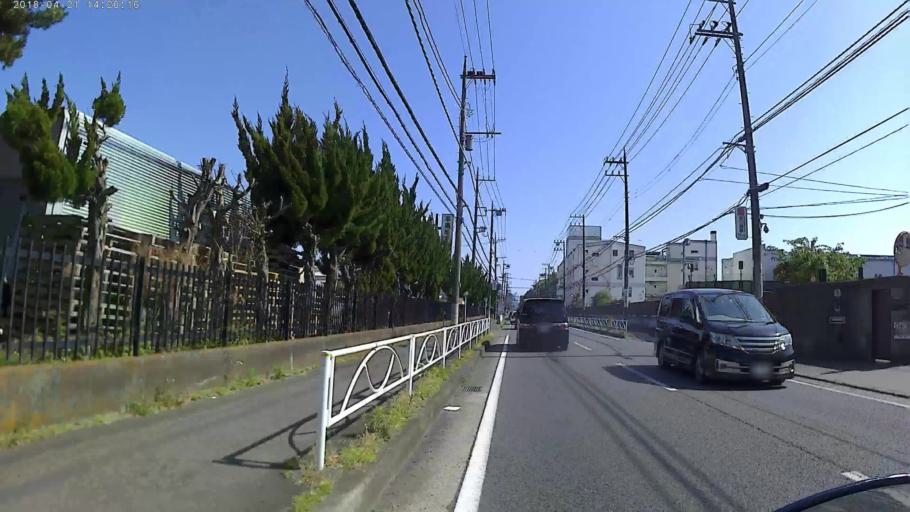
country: JP
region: Kanagawa
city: Hiratsuka
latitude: 35.3477
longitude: 139.3440
